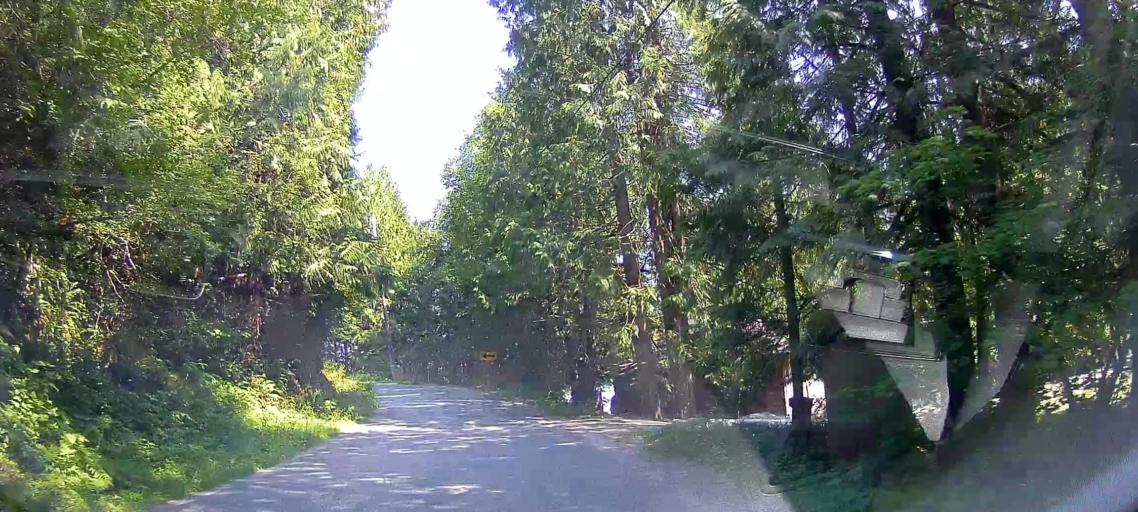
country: US
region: Washington
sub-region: Snohomish County
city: Arlington Heights
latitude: 48.3259
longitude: -122.0369
